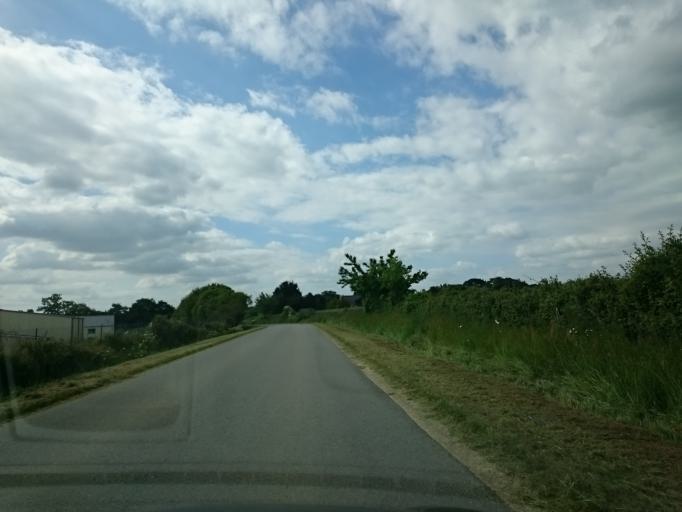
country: FR
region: Brittany
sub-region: Departement d'Ille-et-Vilaine
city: Crevin
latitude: 47.9613
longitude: -1.6831
